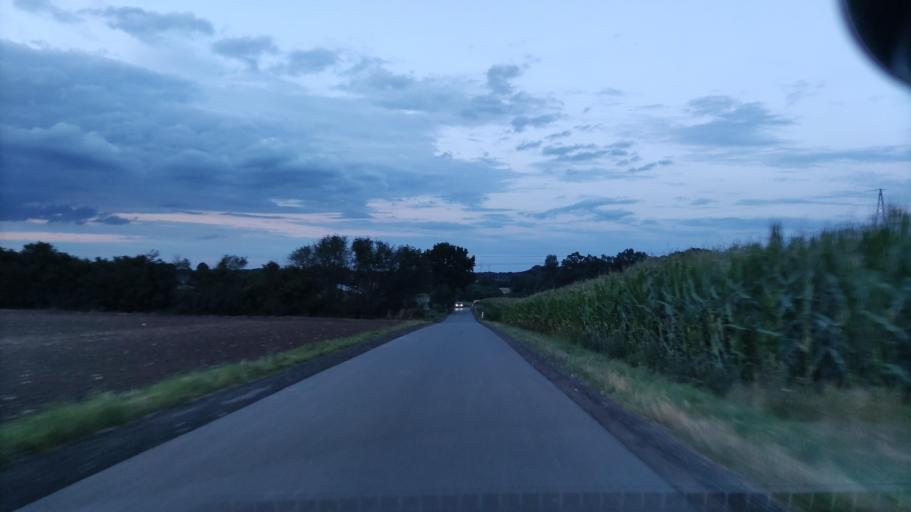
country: DE
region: Schleswig-Holstein
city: Kruzen
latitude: 53.3947
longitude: 10.5207
